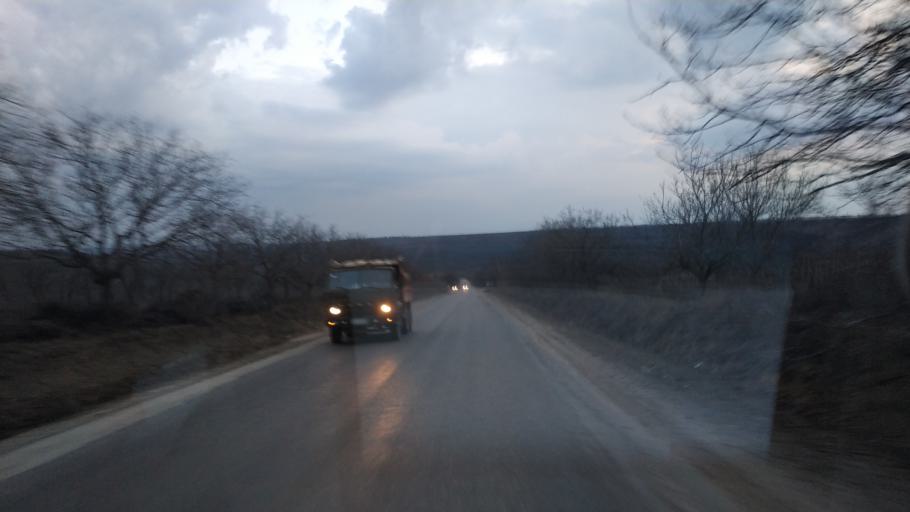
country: MD
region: Anenii Noi
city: Anenii Noi
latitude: 46.9598
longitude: 29.2840
